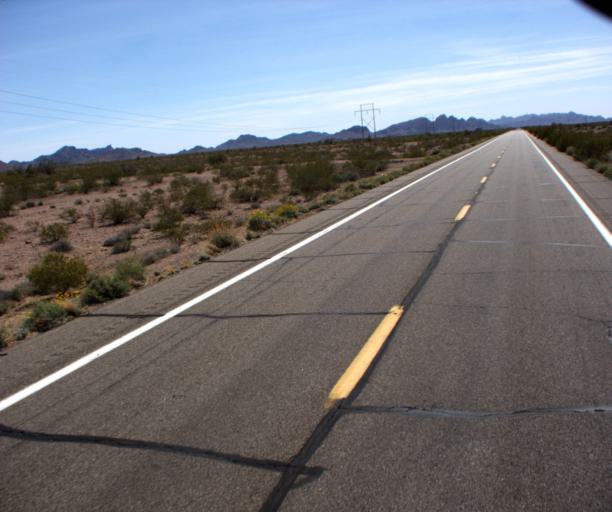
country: US
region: Arizona
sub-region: La Paz County
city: Quartzsite
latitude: 33.3797
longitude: -114.2172
